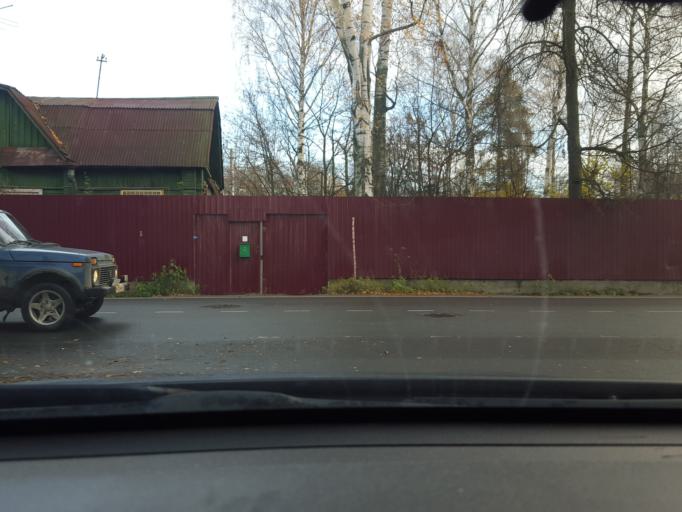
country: RU
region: St.-Petersburg
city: Shuvalovo
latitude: 60.0428
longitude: 30.2985
